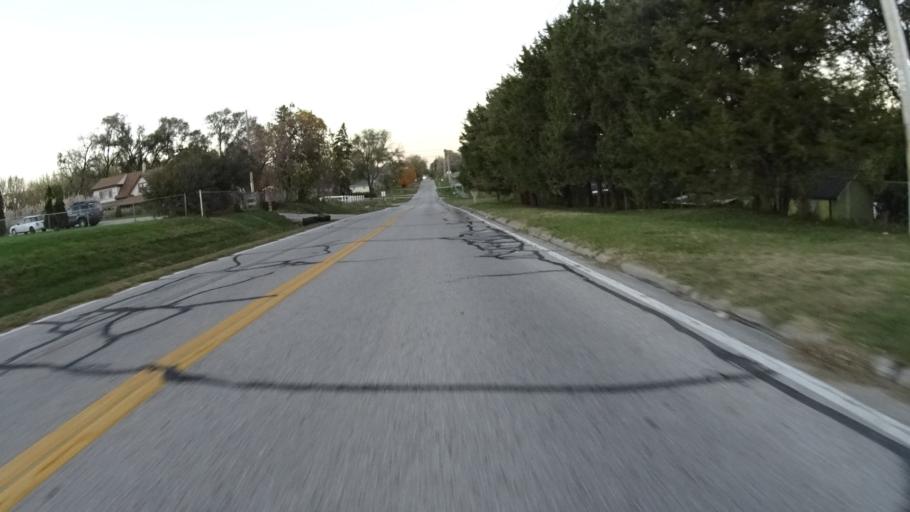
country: US
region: Nebraska
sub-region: Sarpy County
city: Offutt Air Force Base
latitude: 41.1731
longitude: -95.9526
